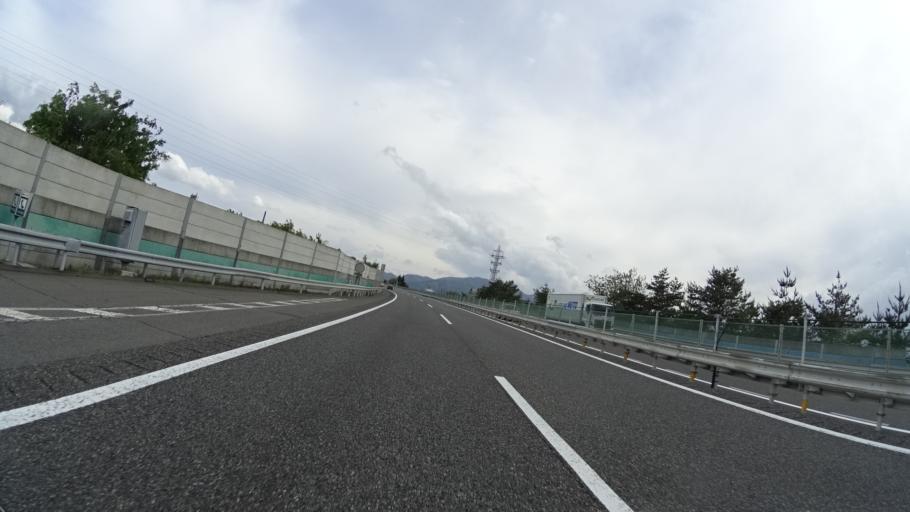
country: JP
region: Nagano
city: Shiojiri
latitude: 36.1392
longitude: 137.9669
